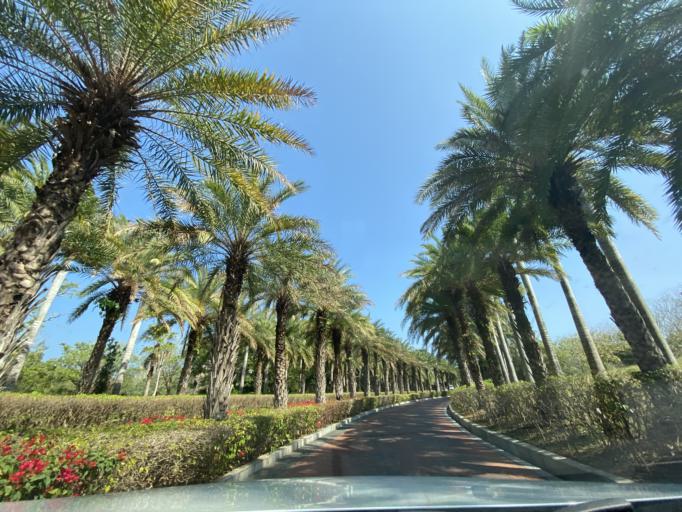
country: CN
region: Hainan
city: Haitangwan
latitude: 18.3488
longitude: 109.7344
